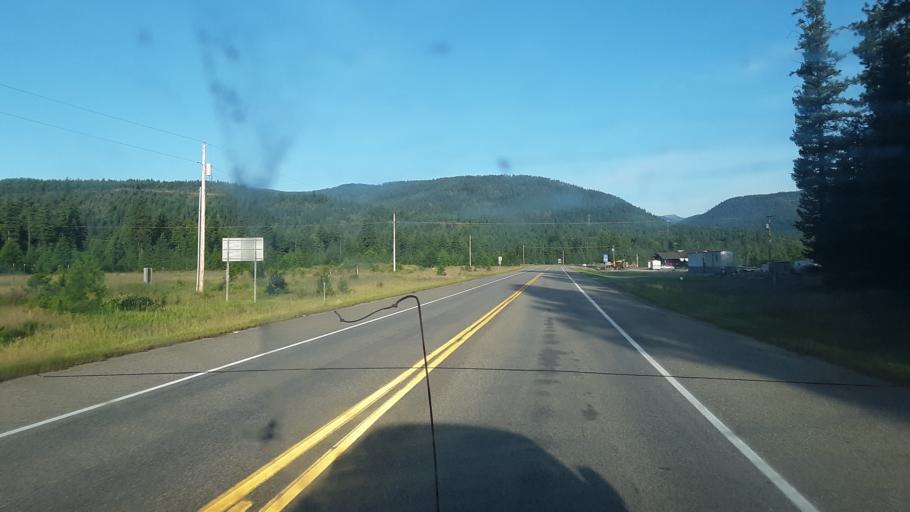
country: US
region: Montana
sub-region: Lincoln County
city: Libby
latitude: 48.4376
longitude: -115.8536
